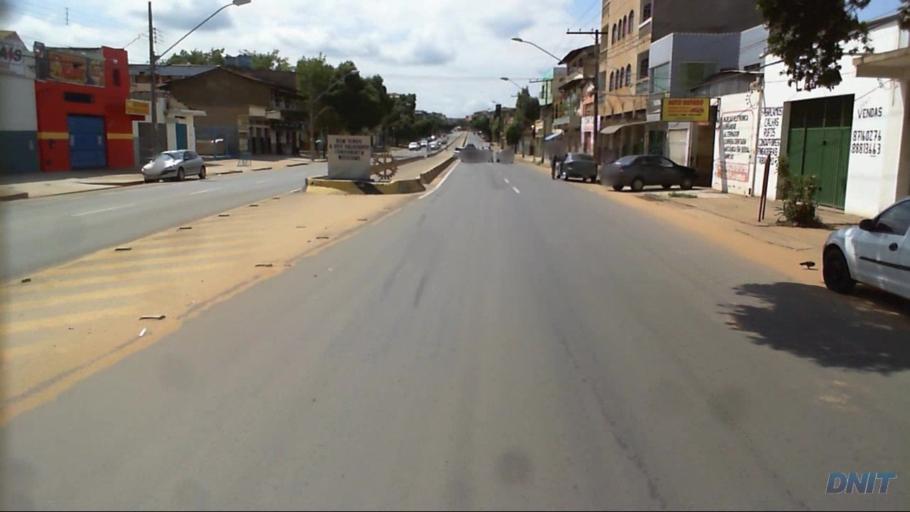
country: BR
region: Minas Gerais
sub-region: Governador Valadares
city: Governador Valadares
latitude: -18.8840
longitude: -41.9674
